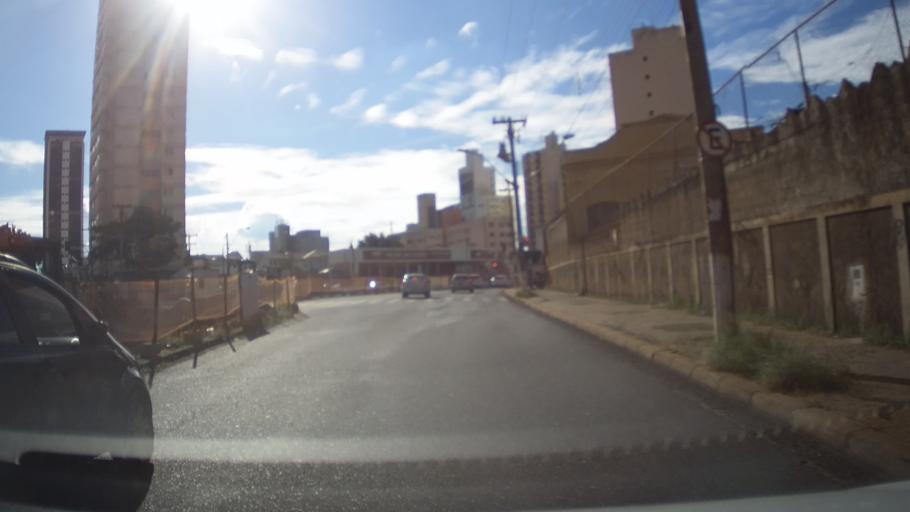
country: BR
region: Sao Paulo
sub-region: Campinas
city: Campinas
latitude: -22.9028
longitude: -47.0667
